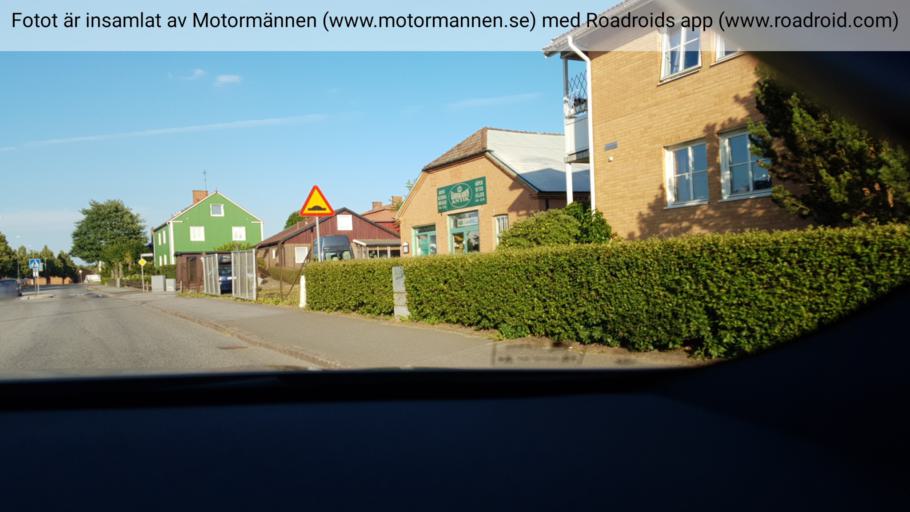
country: SE
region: Vaestra Goetaland
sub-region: Skara Kommun
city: Skara
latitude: 58.3829
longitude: 13.4456
